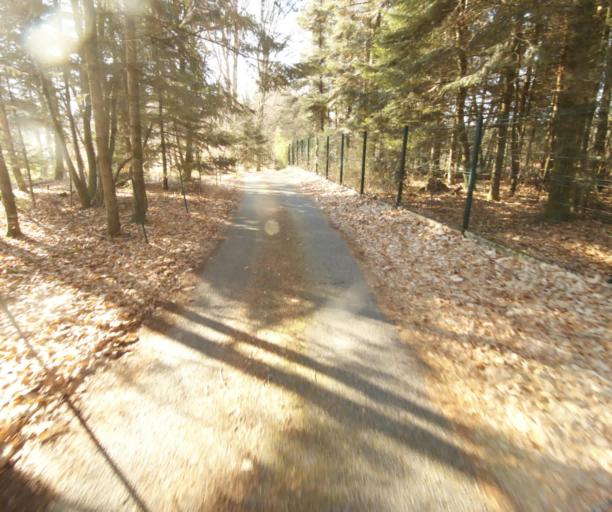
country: FR
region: Limousin
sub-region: Departement de la Correze
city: Correze
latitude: 45.3248
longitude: 1.8735
